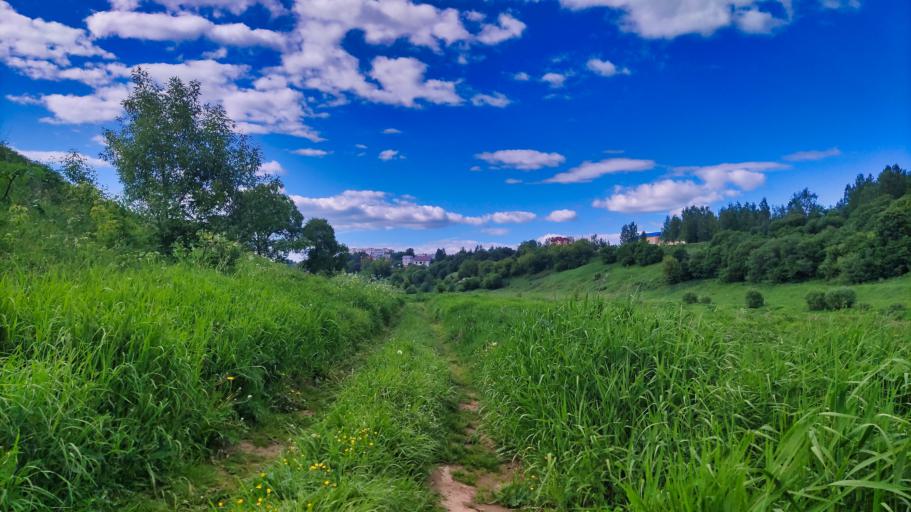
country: RU
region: Tverskaya
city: Rzhev
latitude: 56.2481
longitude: 34.3496
